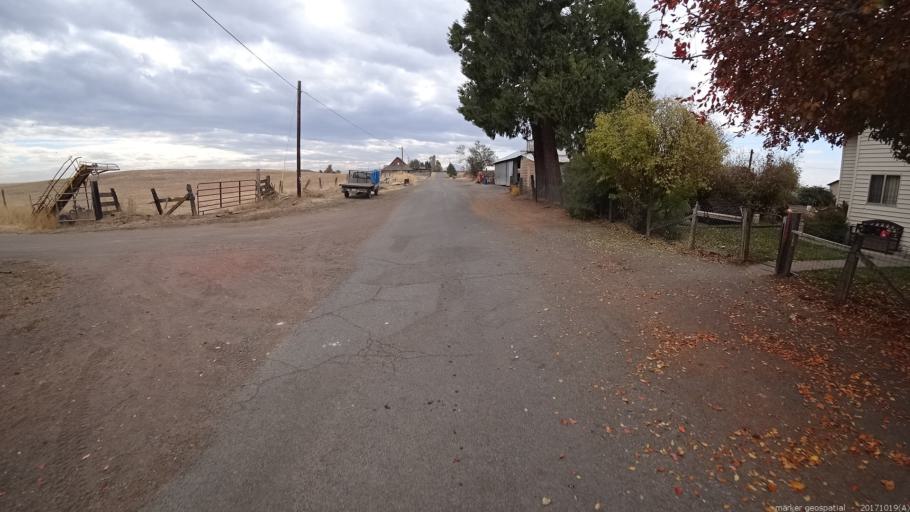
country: US
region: California
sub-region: Shasta County
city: Burney
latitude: 41.0468
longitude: -121.3751
